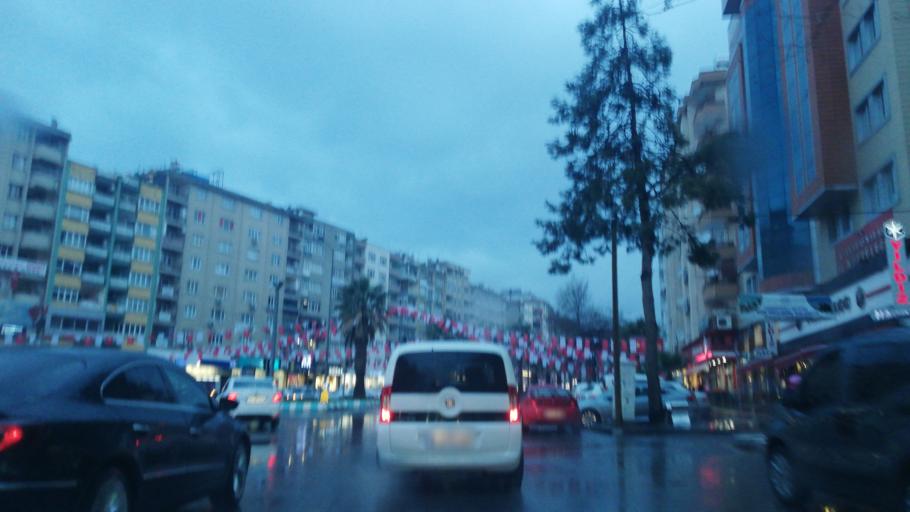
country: TR
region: Kahramanmaras
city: Kahramanmaras
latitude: 37.5747
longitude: 36.9335
